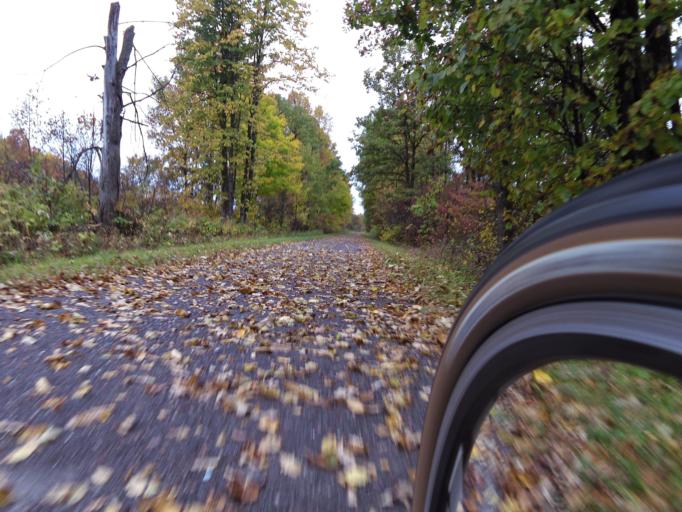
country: CA
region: Quebec
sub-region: Outaouais
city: Shawville
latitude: 45.6968
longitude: -76.5780
